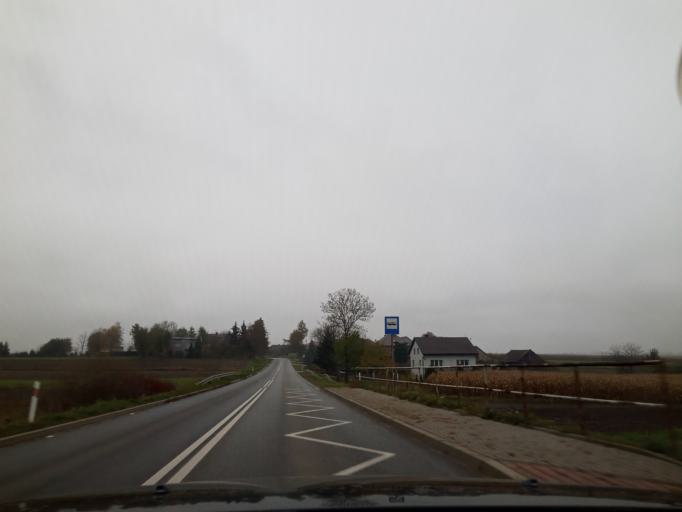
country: PL
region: Lesser Poland Voivodeship
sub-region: Powiat proszowicki
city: Klimontow
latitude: 50.2130
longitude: 20.3118
